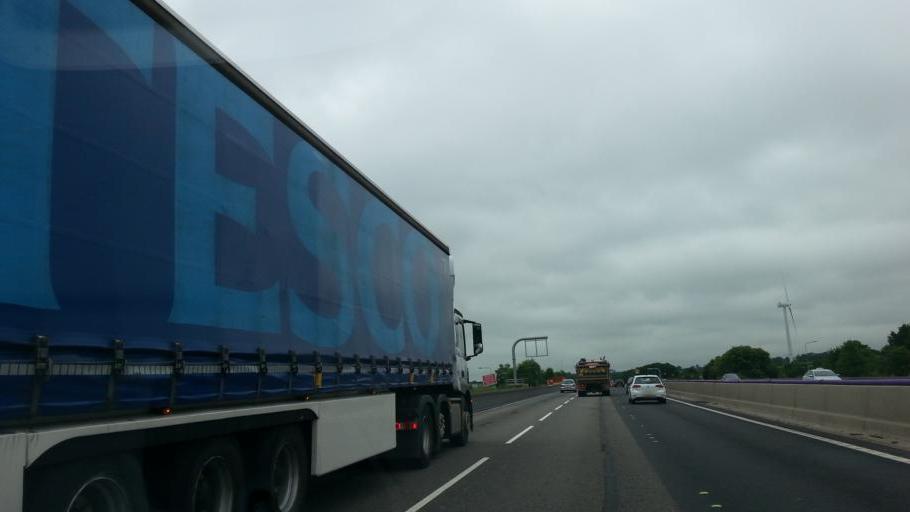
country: GB
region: England
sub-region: Northamptonshire
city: Long Buckby
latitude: 52.3540
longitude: -1.1550
